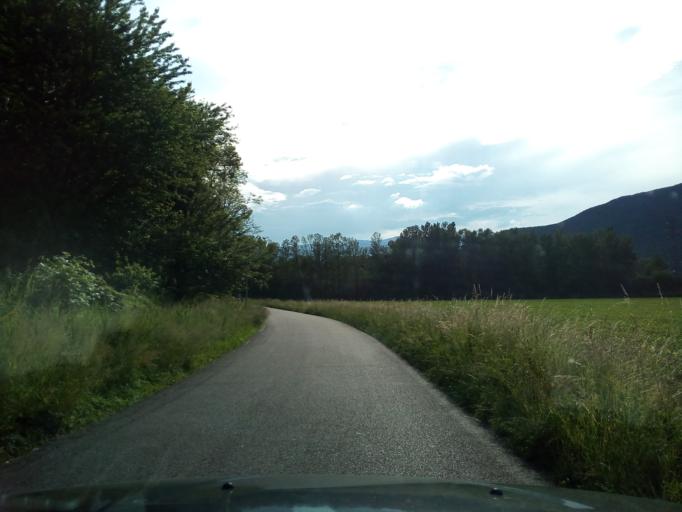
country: FR
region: Rhone-Alpes
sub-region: Departement de l'Isere
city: Corenc
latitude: 45.2016
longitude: 5.7736
